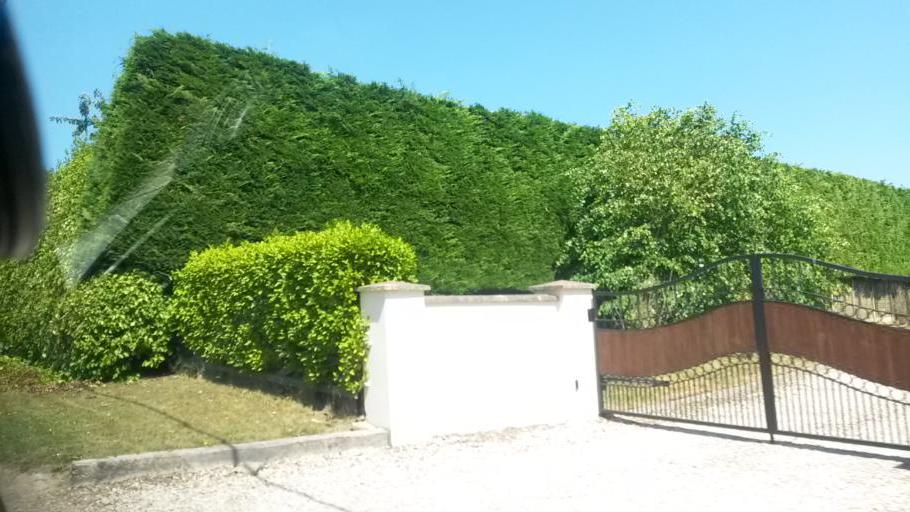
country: IE
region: Leinster
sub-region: An Mhi
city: Ashbourne
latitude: 53.5220
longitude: -6.3156
